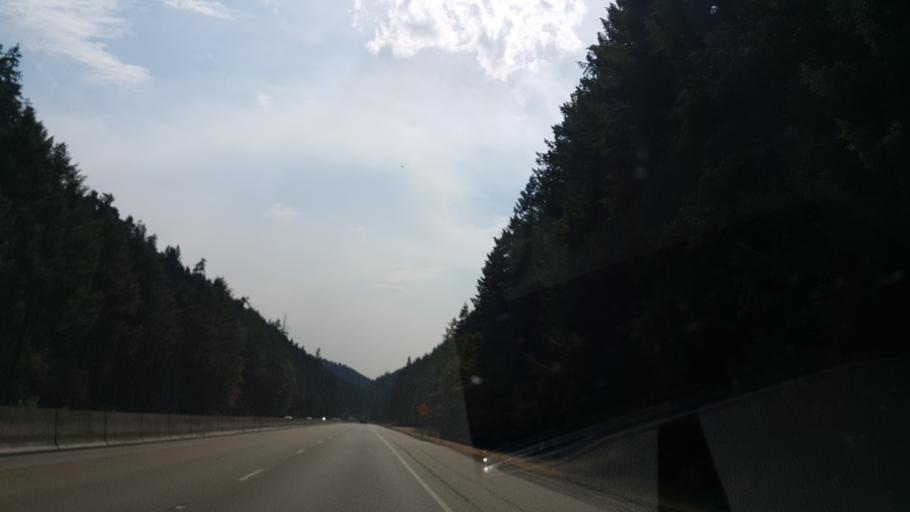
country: US
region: Oregon
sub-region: Douglas County
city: Canyonville
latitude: 42.8850
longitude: -123.2404
